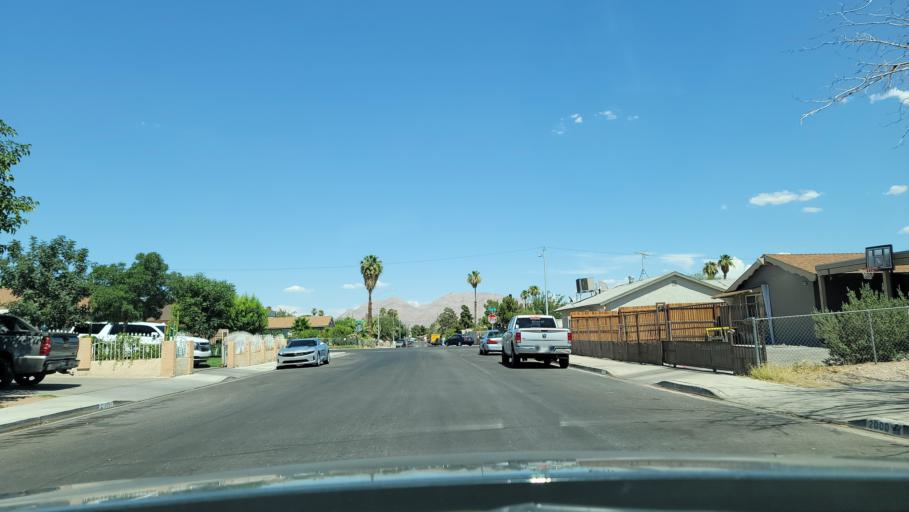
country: US
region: Nevada
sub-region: Clark County
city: North Las Vegas
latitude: 36.1838
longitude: -115.1212
